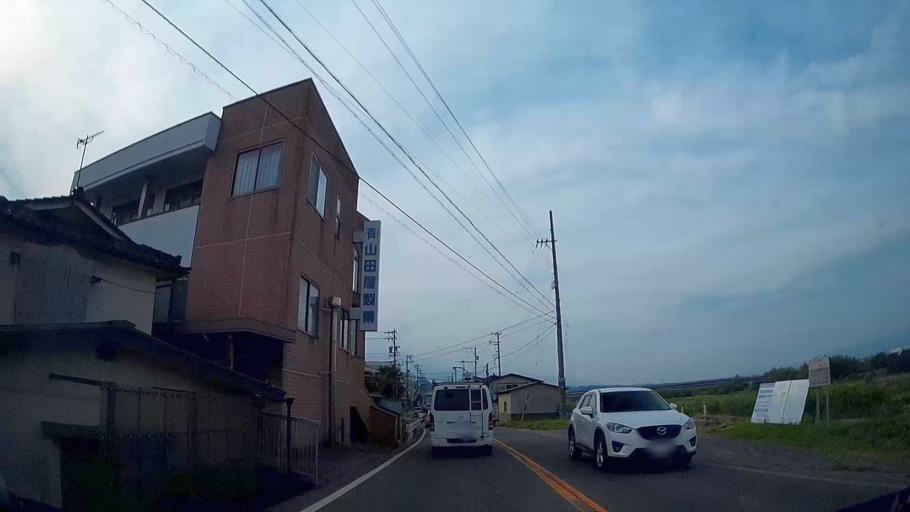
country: JP
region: Nagano
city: Ina
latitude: 35.8057
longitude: 137.9448
